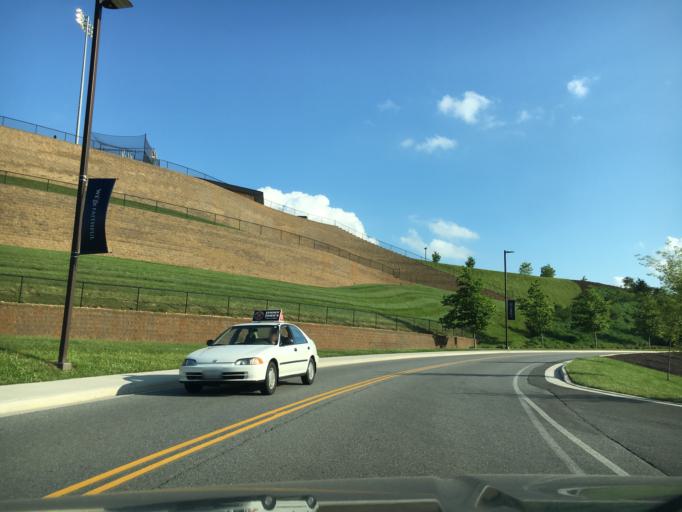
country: US
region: Virginia
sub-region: City of Lynchburg
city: West Lynchburg
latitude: 37.3575
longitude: -79.1782
